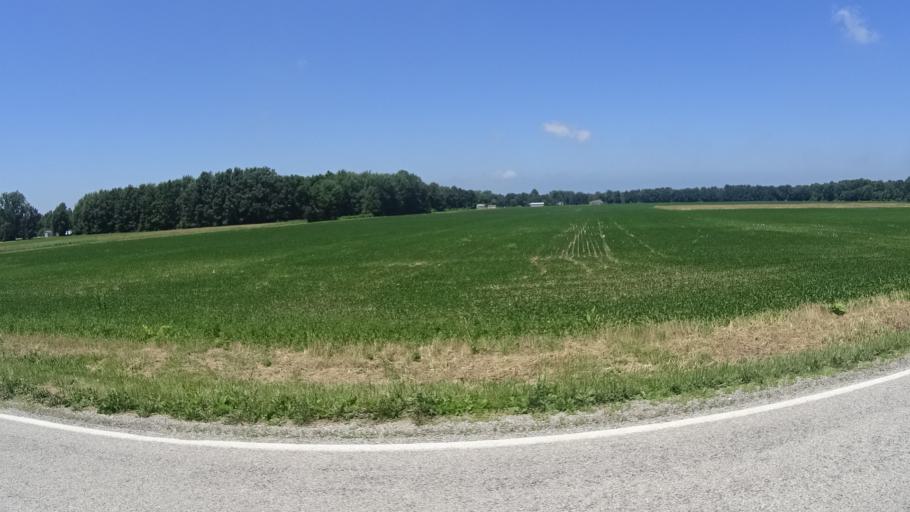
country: US
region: Ohio
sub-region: Lorain County
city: Vermilion
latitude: 41.3465
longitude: -82.4206
